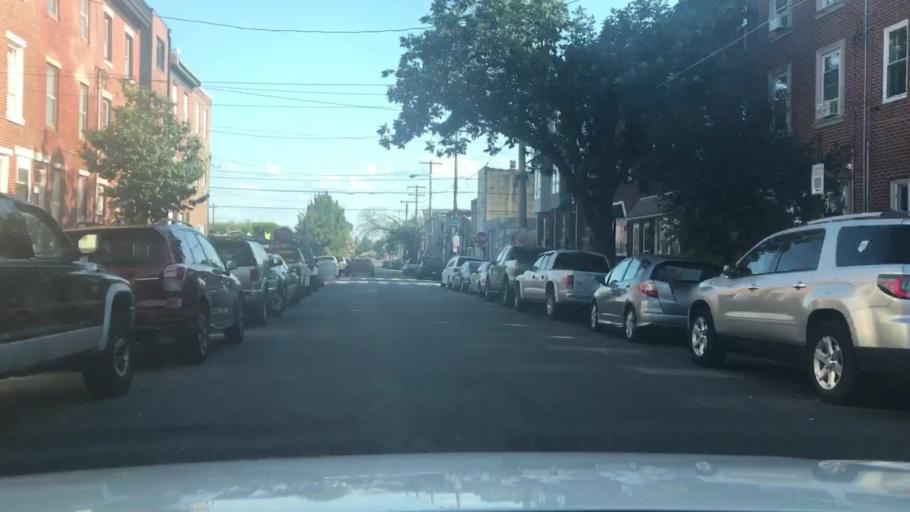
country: US
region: Pennsylvania
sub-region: Philadelphia County
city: Philadelphia
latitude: 39.9789
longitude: -75.1223
